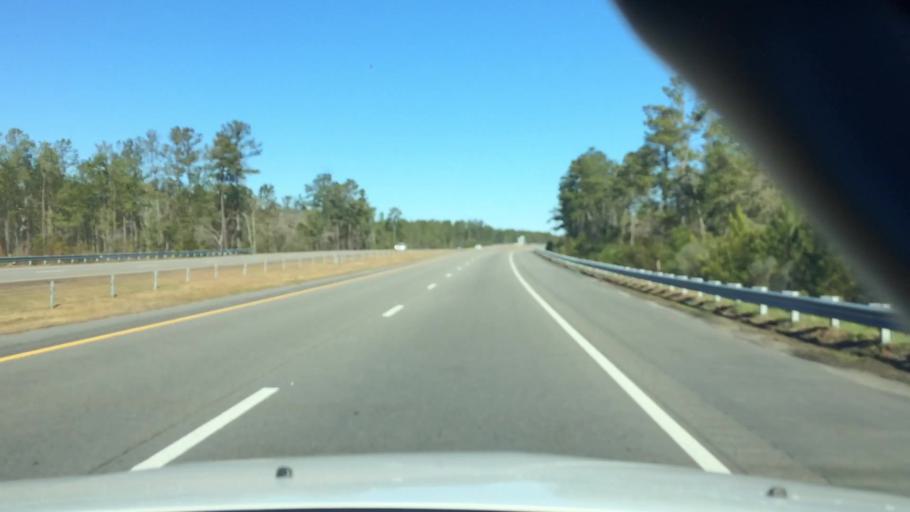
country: US
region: North Carolina
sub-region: Brunswick County
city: Leland
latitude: 34.2131
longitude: -78.0764
